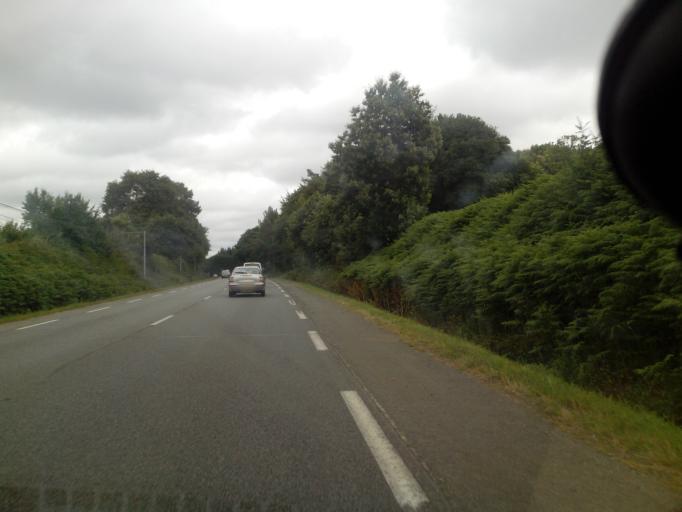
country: FR
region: Brittany
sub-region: Departement du Morbihan
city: Hennebont
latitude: 47.7695
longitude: -3.2768
